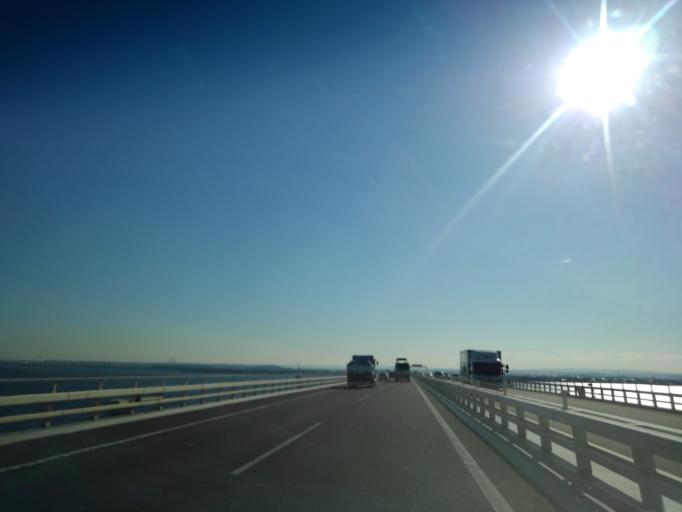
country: JP
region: Chiba
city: Kisarazu
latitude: 35.4457
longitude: 139.9018
